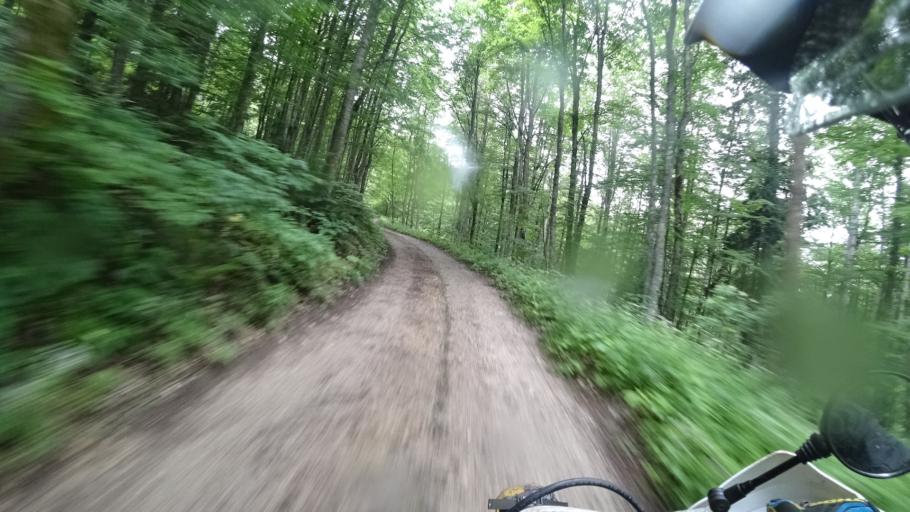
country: HR
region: Primorsko-Goranska
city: Vrbovsko
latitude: 45.2992
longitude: 14.9354
